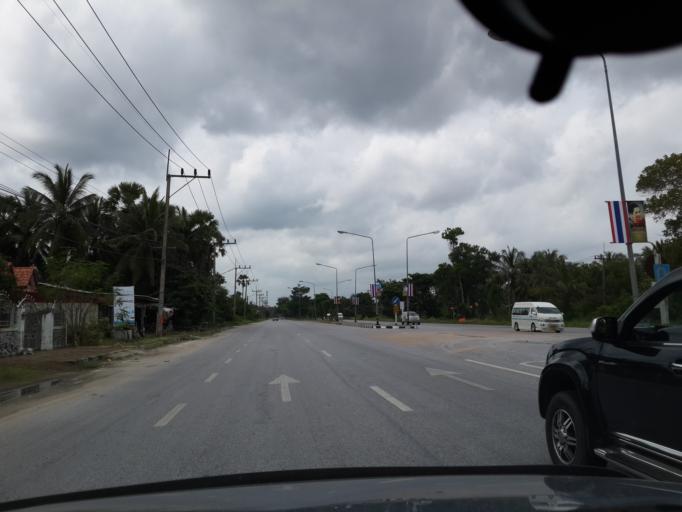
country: TH
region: Pattani
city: Yaring
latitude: 6.8690
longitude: 101.3473
